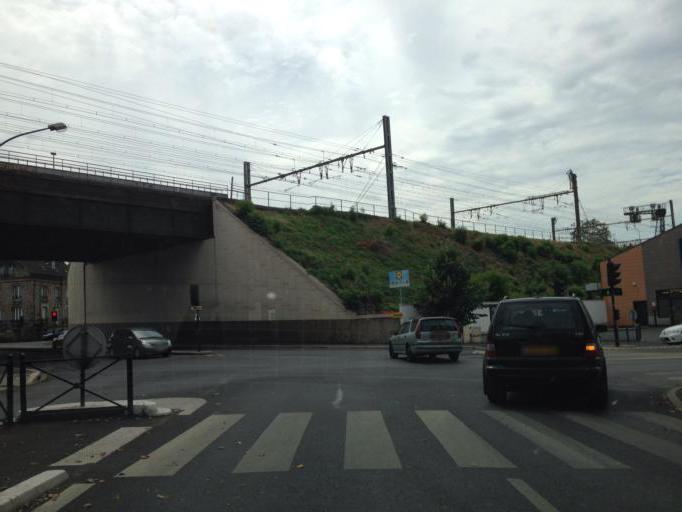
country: FR
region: Ile-de-France
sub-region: Departement des Hauts-de-Seine
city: Issy-les-Moulineaux
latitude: 48.8150
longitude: 2.2783
